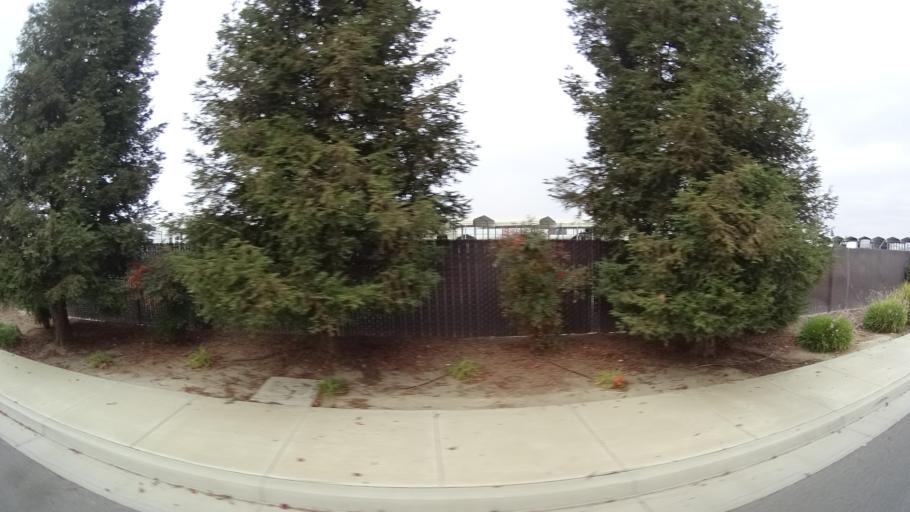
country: US
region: California
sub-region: Kern County
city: Greenfield
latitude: 35.3086
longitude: -119.0708
